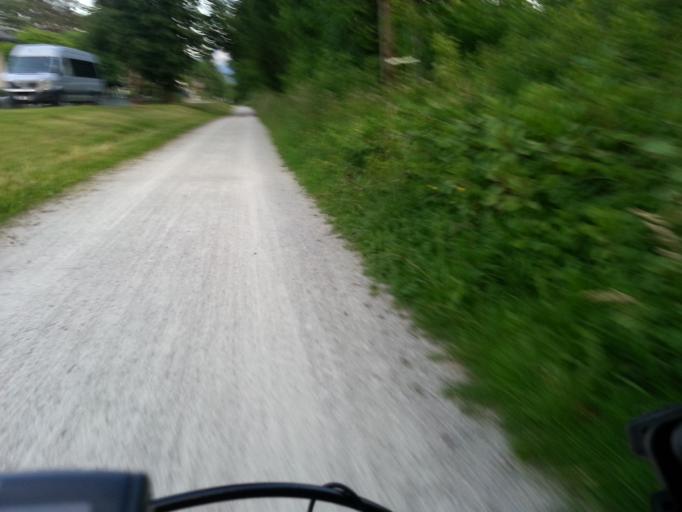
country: AT
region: Salzburg
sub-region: Politischer Bezirk Salzburg-Umgebung
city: Elsbethen
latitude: 47.7448
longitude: 13.0816
